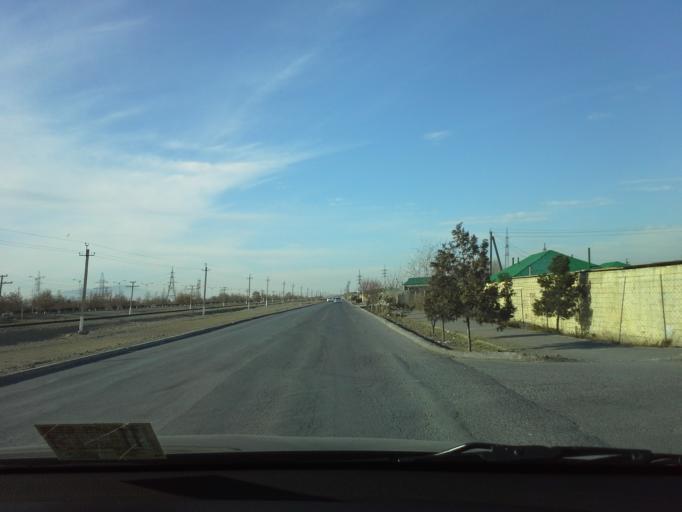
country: TM
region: Ahal
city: Abadan
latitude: 38.0615
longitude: 58.1723
